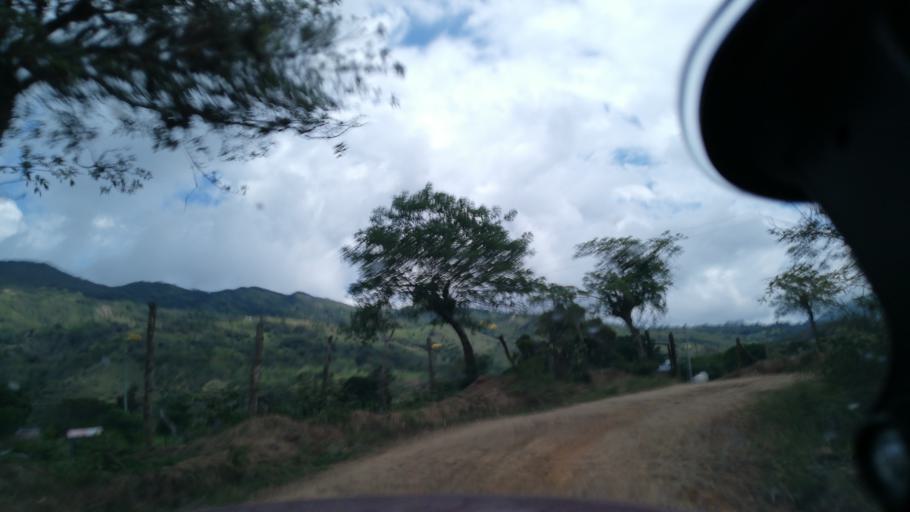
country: CO
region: Cundinamarca
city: Quipile
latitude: 4.8107
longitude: -74.6204
